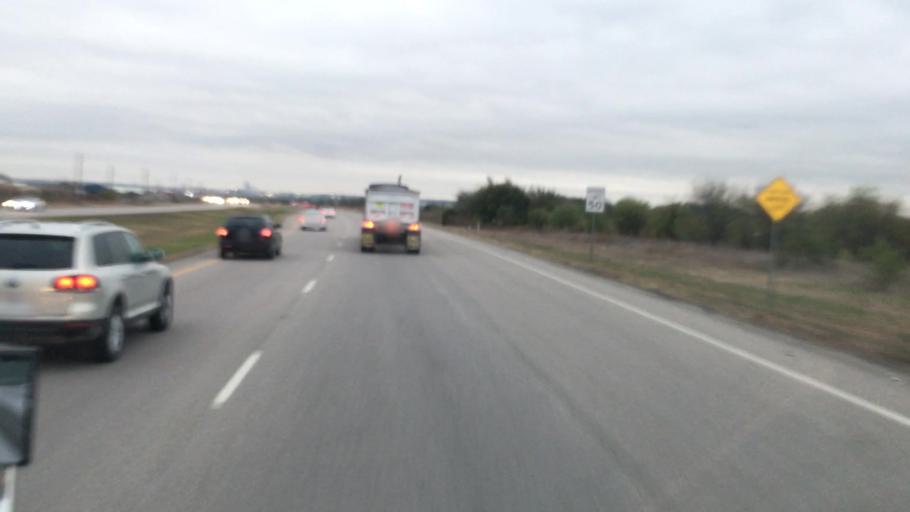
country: US
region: Texas
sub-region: Johnson County
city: Venus
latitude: 32.4361
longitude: -97.1023
